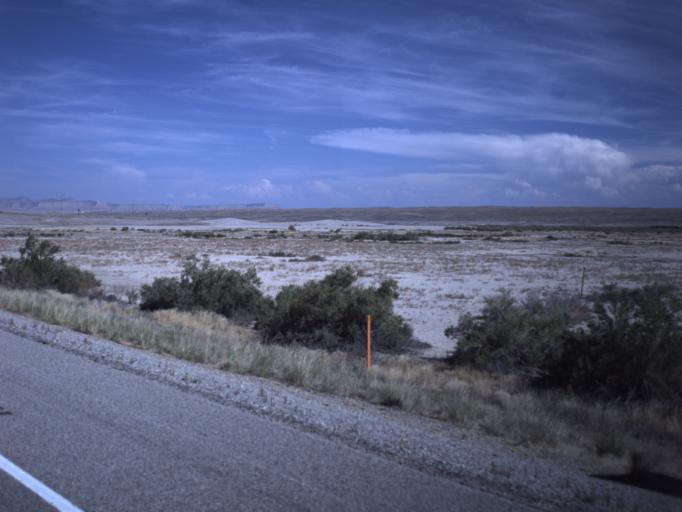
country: US
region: Utah
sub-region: Carbon County
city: East Carbon City
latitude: 38.9799
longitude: -110.2371
